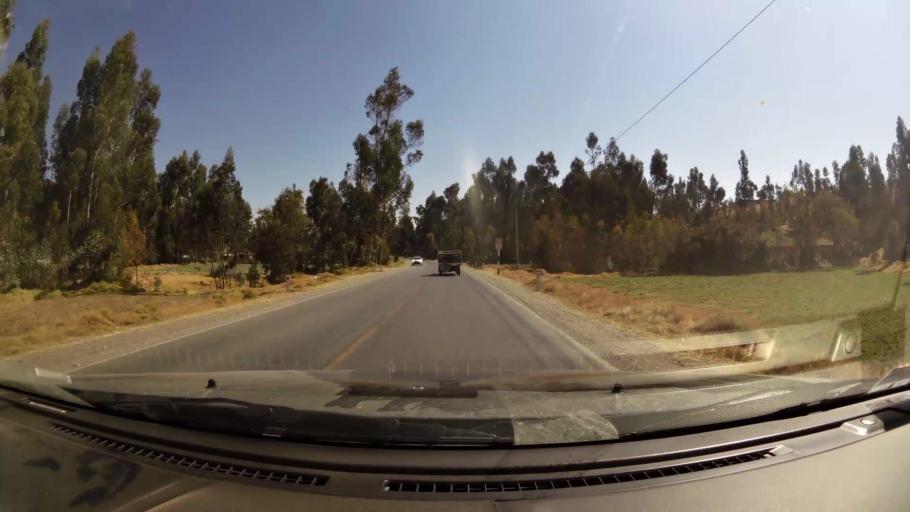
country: PE
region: Junin
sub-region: Provincia de Concepcion
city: Concepcion
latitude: -11.9306
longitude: -75.3142
